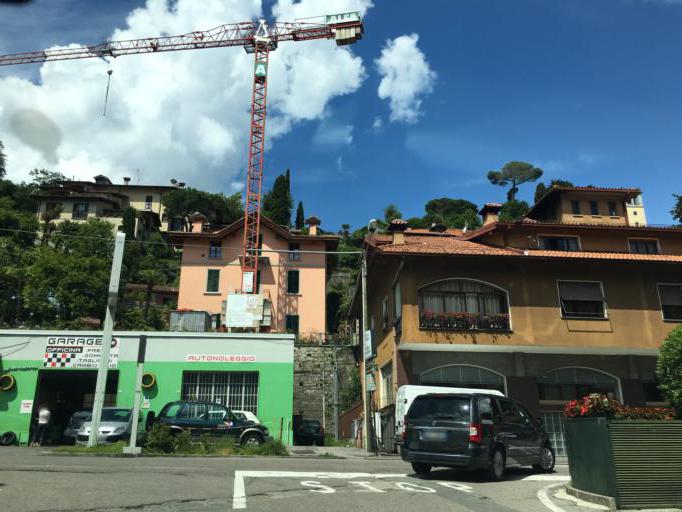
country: IT
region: Lombardy
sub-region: Provincia di Como
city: Menaggio
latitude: 46.0175
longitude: 9.2364
